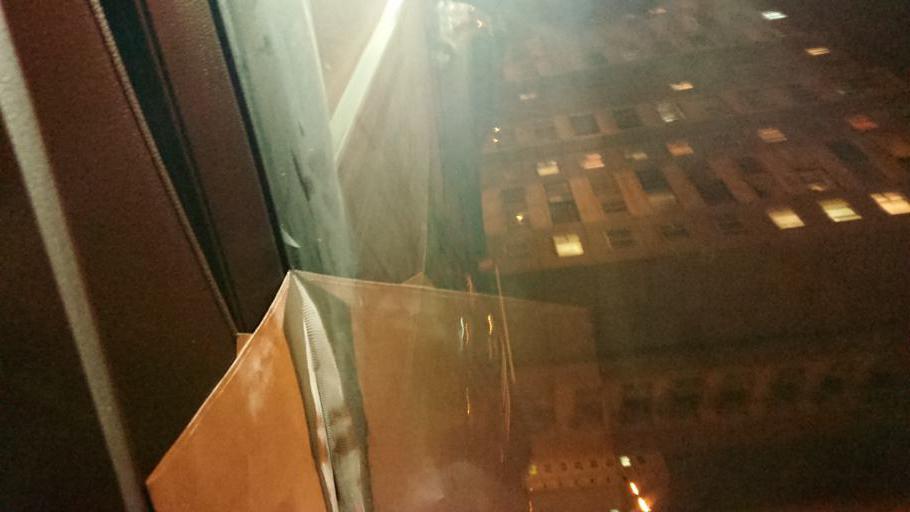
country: BY
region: Minsk
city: Minsk
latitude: 53.9343
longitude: 27.5942
